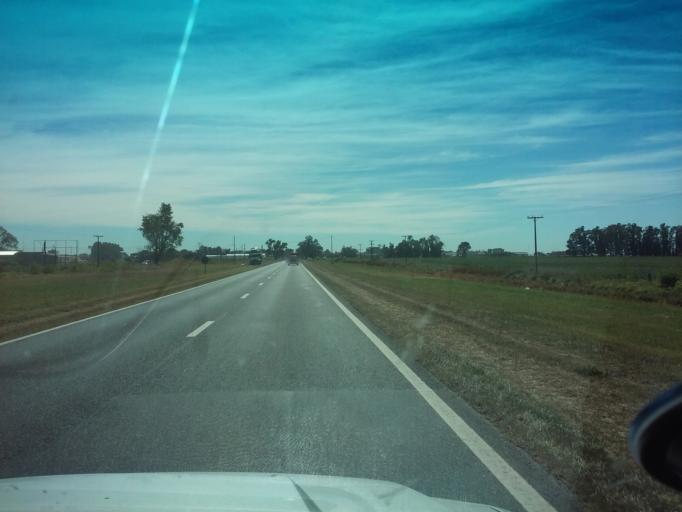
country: AR
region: Buenos Aires
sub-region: Partido de Bragado
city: Bragado
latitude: -35.1536
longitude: -60.4714
